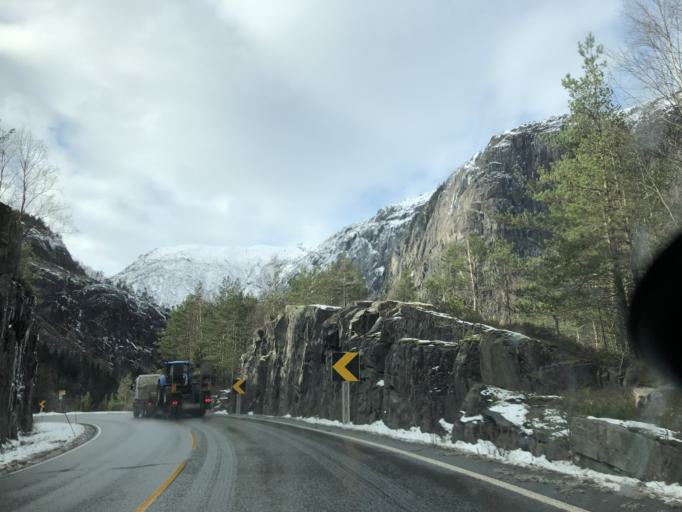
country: NO
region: Rogaland
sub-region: Sauda
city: Sauda
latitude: 59.8752
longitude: 6.4057
